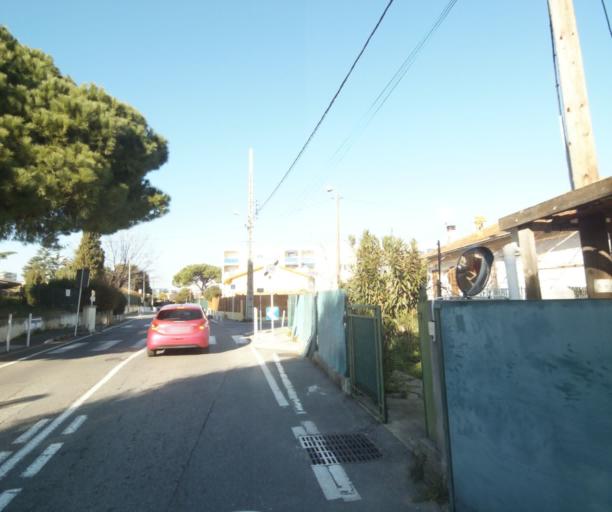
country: FR
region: Provence-Alpes-Cote d'Azur
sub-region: Departement des Alpes-Maritimes
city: Biot
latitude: 43.6055
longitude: 7.1211
